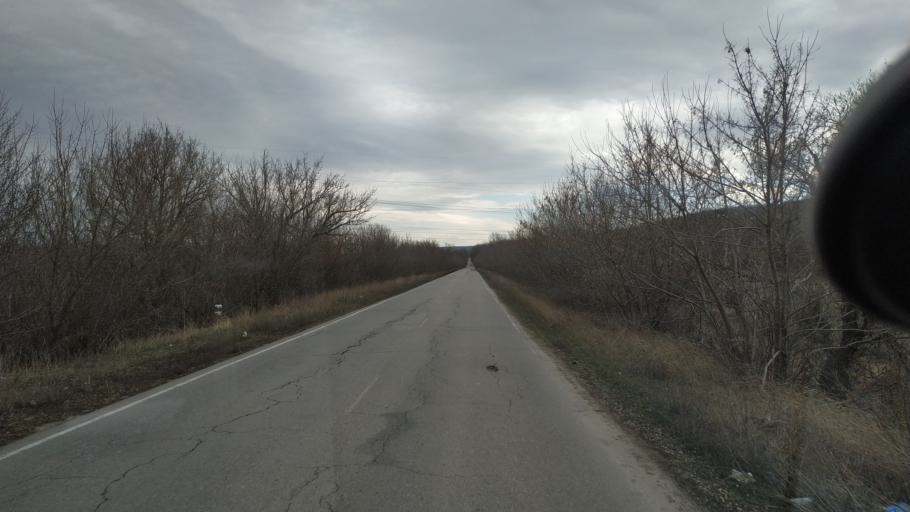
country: MD
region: Chisinau
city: Vadul lui Voda
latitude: 47.1121
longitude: 29.0597
